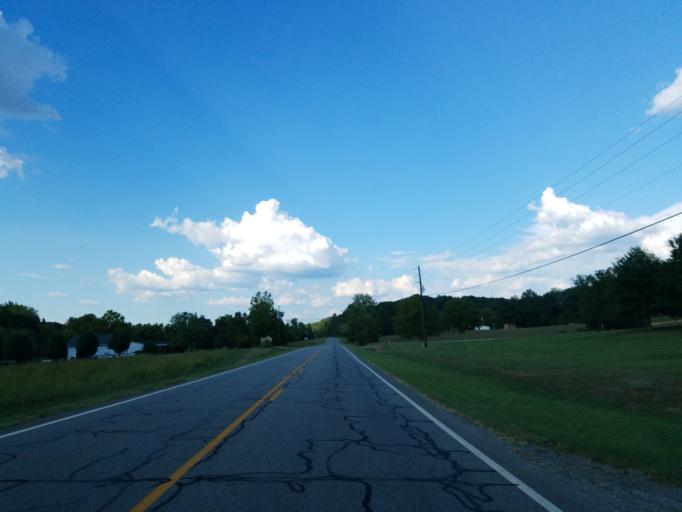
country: US
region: Georgia
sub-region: Bartow County
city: Rydal
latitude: 34.5173
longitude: -84.7094
